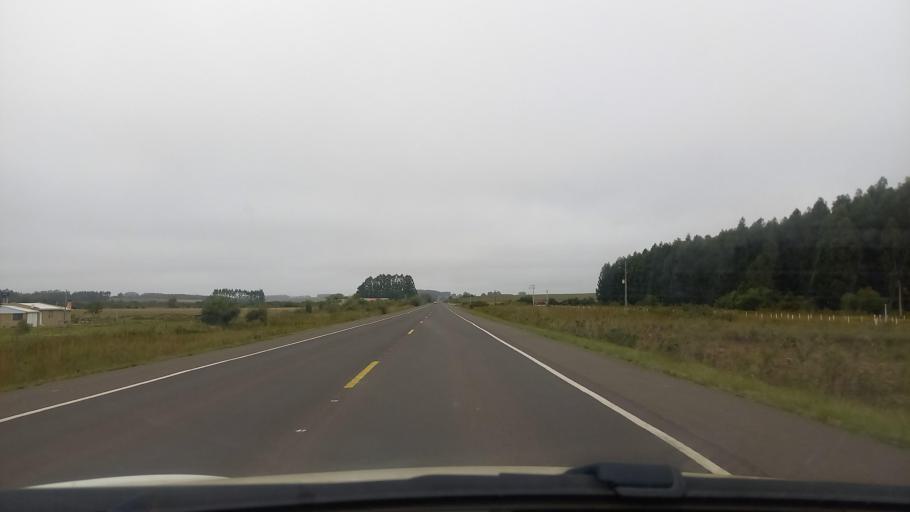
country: BR
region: Rio Grande do Sul
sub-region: Rosario Do Sul
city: Rosario do Sul
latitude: -30.2980
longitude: -54.9897
